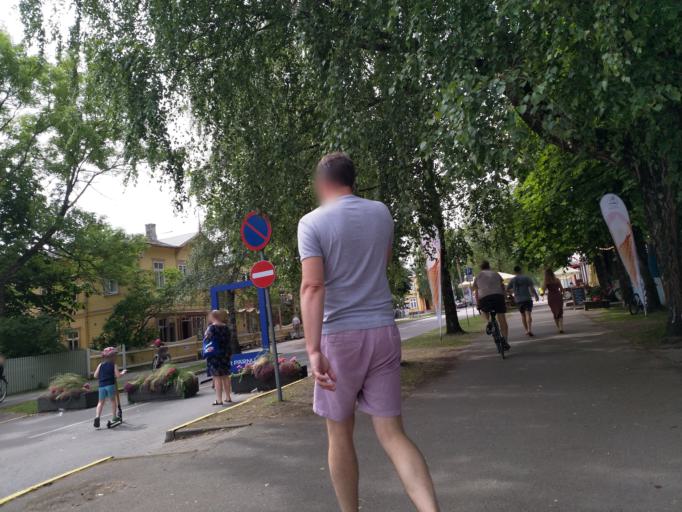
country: EE
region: Paernumaa
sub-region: Paernu linn
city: Parnu
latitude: 58.3811
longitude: 24.5021
